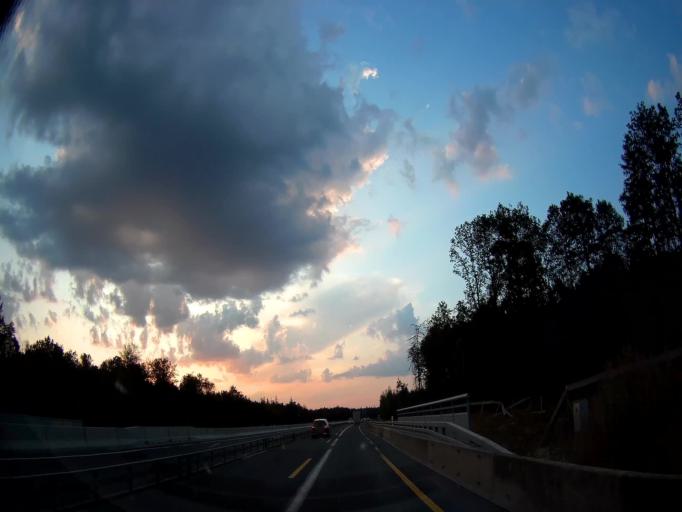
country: DE
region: Bavaria
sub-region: Regierungsbezirk Unterfranken
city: Esselbach
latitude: 49.8384
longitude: 9.5130
